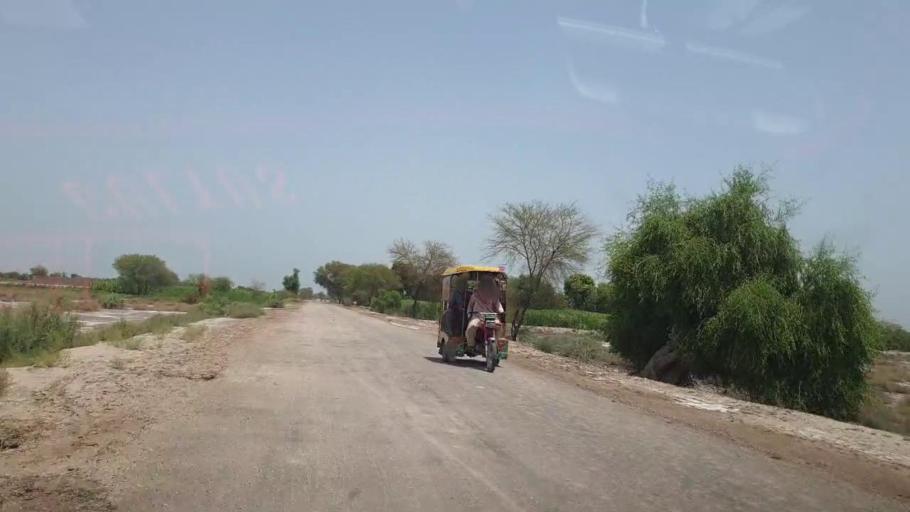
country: PK
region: Sindh
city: Daulatpur
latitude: 26.3894
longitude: 68.0970
